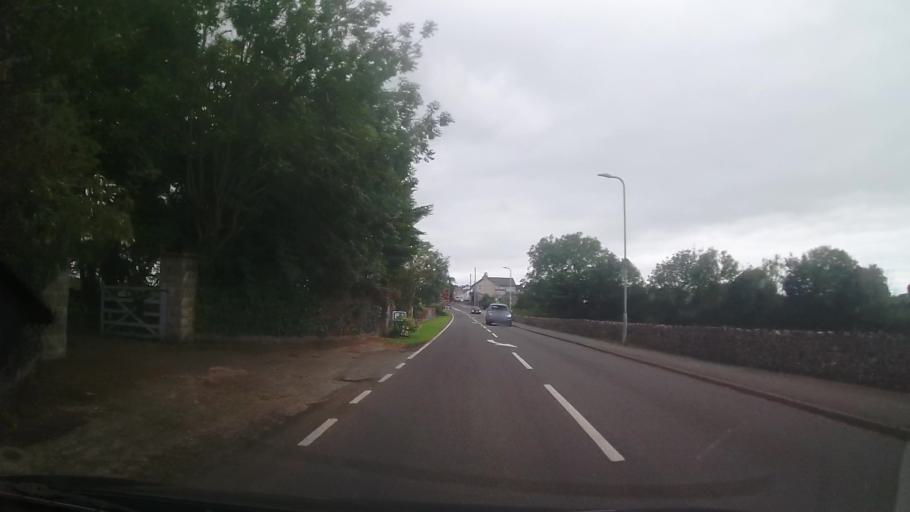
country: GB
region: Wales
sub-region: Gwynedd
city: Caernarfon
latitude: 53.1809
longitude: -4.2672
